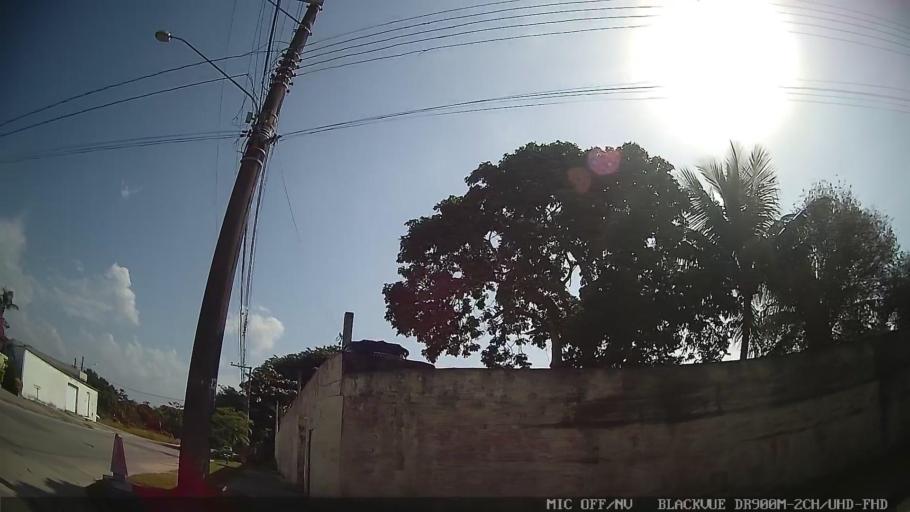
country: BR
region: Sao Paulo
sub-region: Guaruja
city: Guaruja
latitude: -23.9733
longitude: -46.1928
